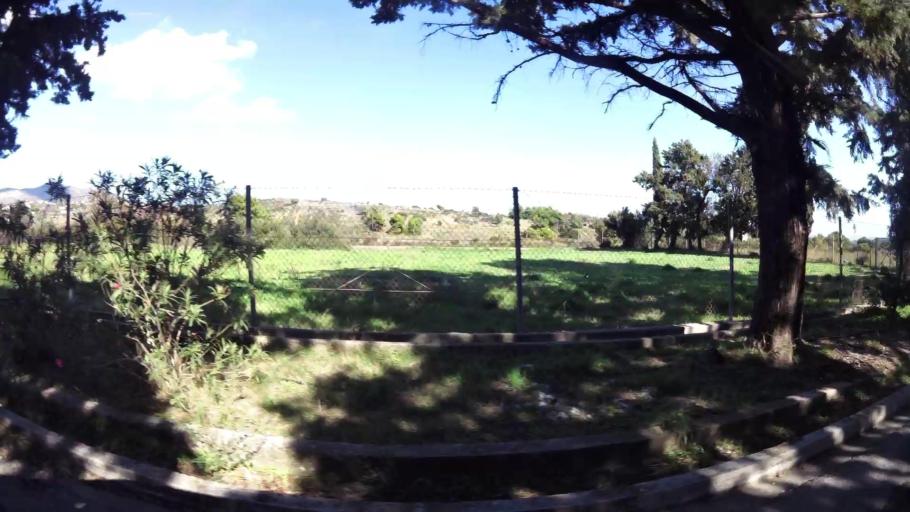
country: GR
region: Attica
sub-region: Nomarchia Anatolikis Attikis
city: Pikermi
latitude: 38.0101
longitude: 23.9361
